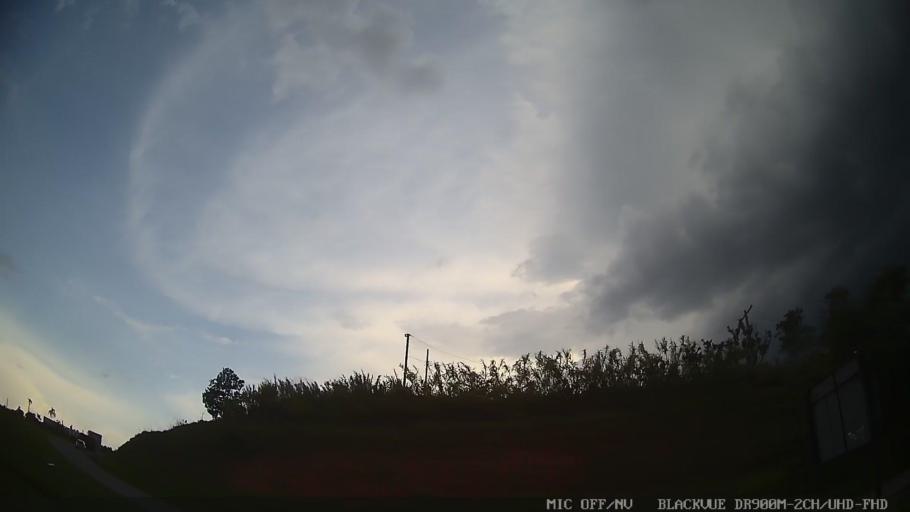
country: BR
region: Sao Paulo
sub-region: Itatiba
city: Itatiba
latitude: -22.9770
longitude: -46.8367
